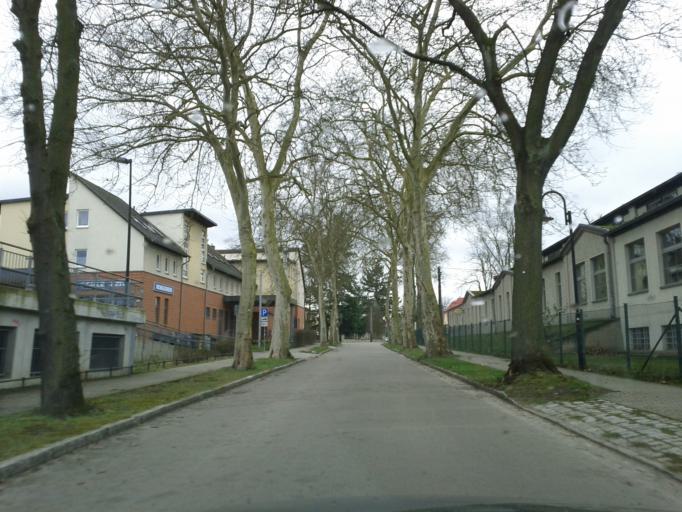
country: DE
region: Brandenburg
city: Woltersdorf
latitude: 52.4512
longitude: 13.7549
